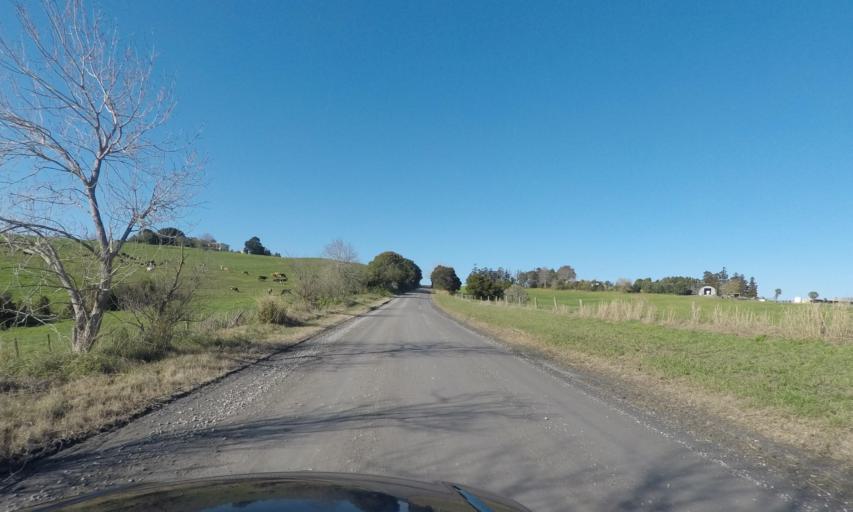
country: NZ
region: Auckland
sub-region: Auckland
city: Wellsford
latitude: -36.1594
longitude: 174.6025
